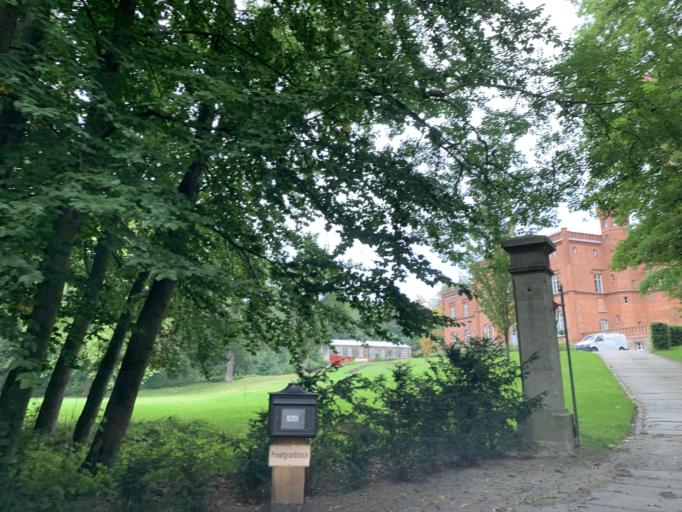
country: DE
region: Mecklenburg-Vorpommern
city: Woldegk
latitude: 53.3339
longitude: 13.6185
